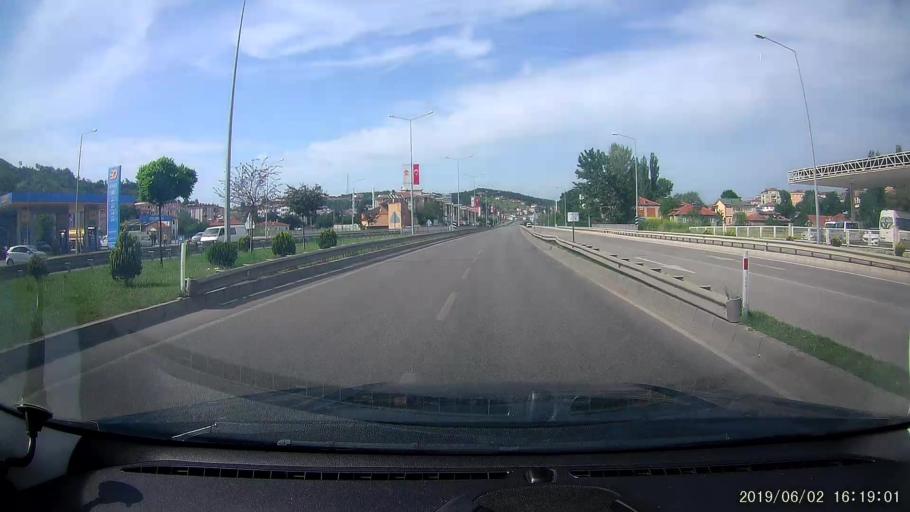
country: TR
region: Samsun
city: Havza
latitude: 40.9623
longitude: 35.6666
